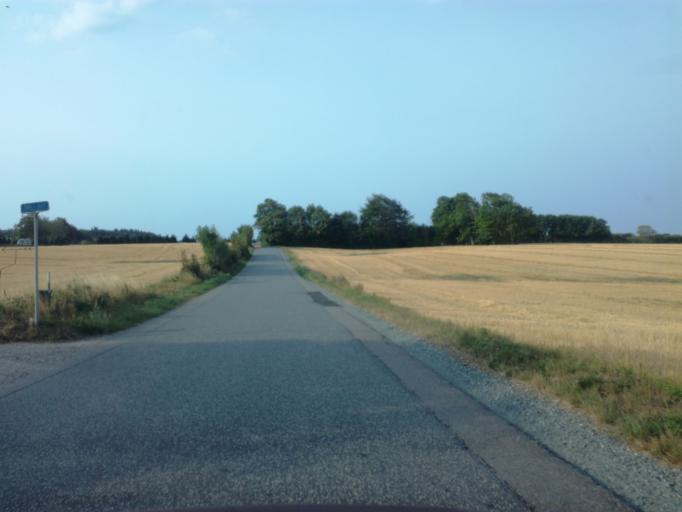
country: DK
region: South Denmark
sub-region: Vejle Kommune
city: Vejle
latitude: 55.6543
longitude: 9.5451
